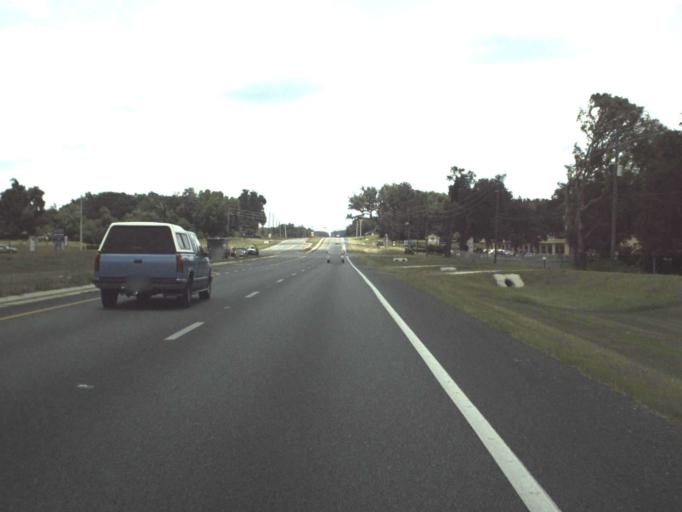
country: US
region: Florida
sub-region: Sumter County
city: Wildwood
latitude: 28.8965
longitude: -82.0369
